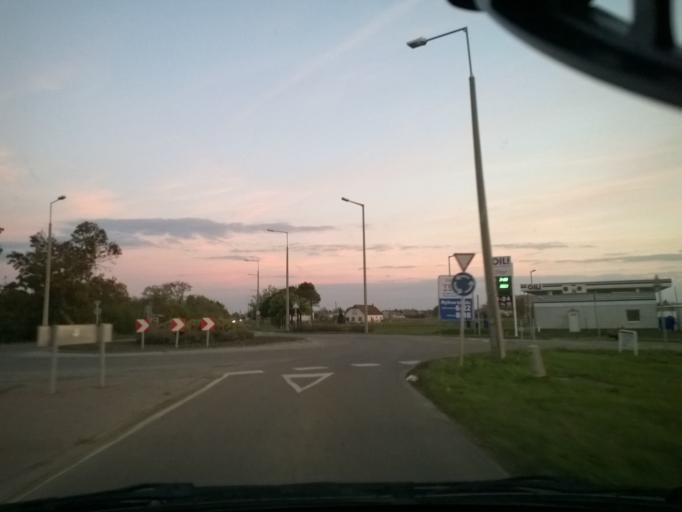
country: HU
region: Csongrad
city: Szentes
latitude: 46.6665
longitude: 20.2363
